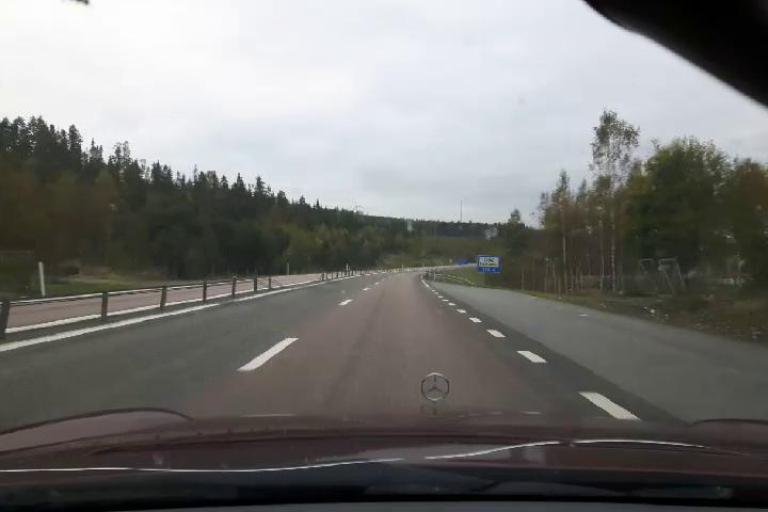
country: SE
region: Vaesternorrland
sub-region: Haernoesands Kommun
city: Haernoesand
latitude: 62.8113
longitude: 17.9610
